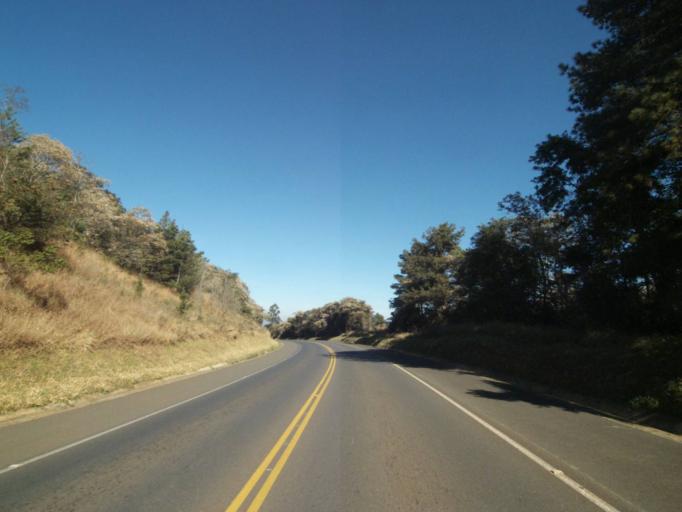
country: BR
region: Parana
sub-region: Tibagi
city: Tibagi
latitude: -24.4079
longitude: -50.3523
